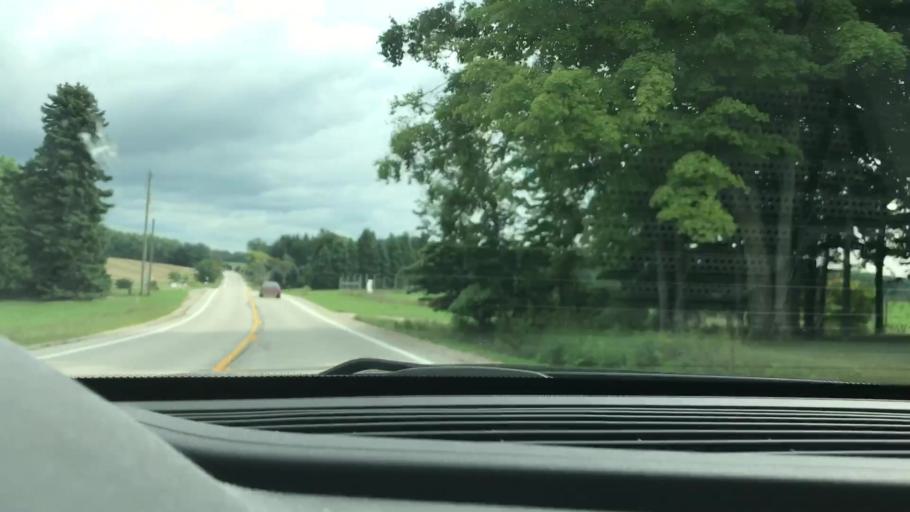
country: US
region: Michigan
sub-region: Antrim County
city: Bellaire
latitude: 45.0973
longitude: -85.3002
